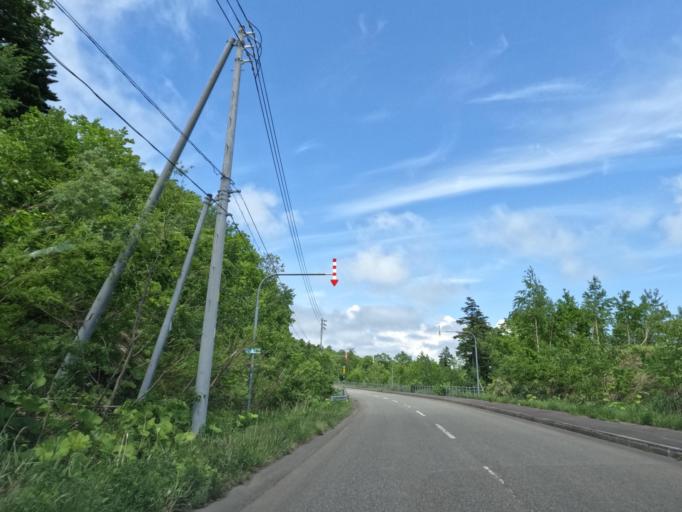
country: JP
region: Hokkaido
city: Tobetsu
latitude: 43.3227
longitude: 141.5698
